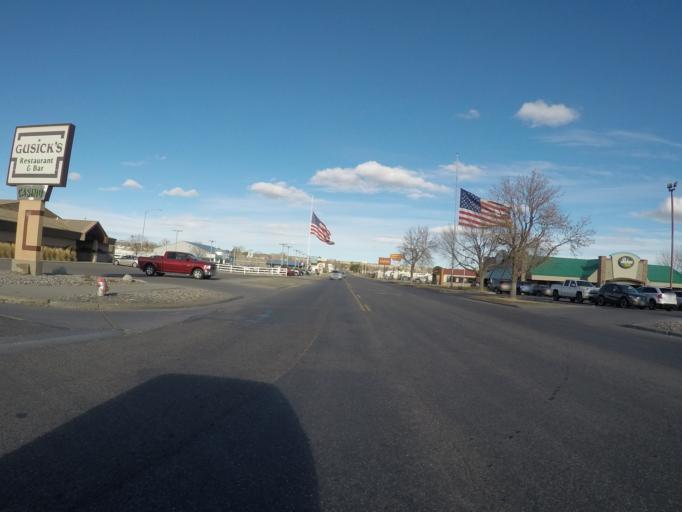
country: US
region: Montana
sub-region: Yellowstone County
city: Billings
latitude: 45.7560
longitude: -108.5667
